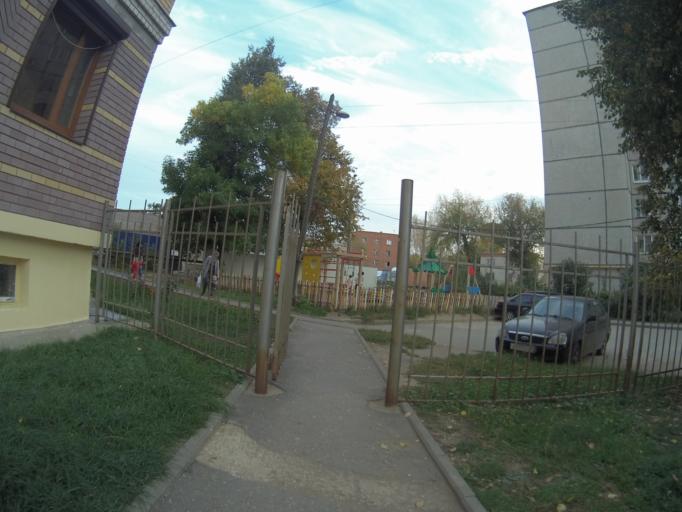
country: RU
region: Vladimir
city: Vladimir
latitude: 56.1427
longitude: 40.3823
